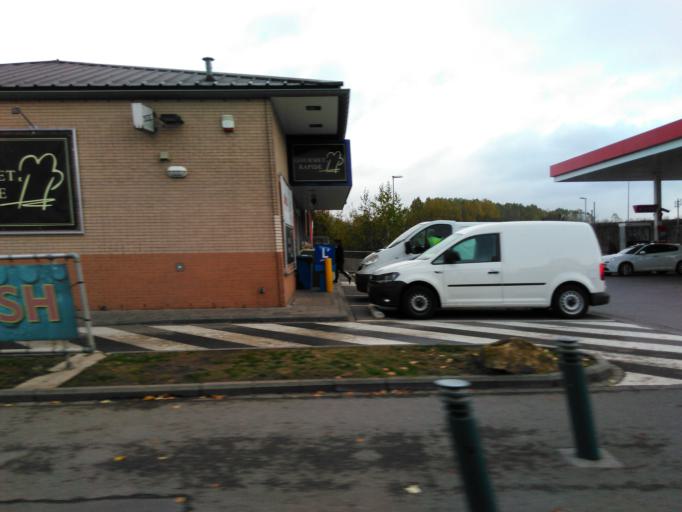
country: FR
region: Lorraine
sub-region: Departement de la Moselle
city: Russange
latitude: 49.5069
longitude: 5.9585
